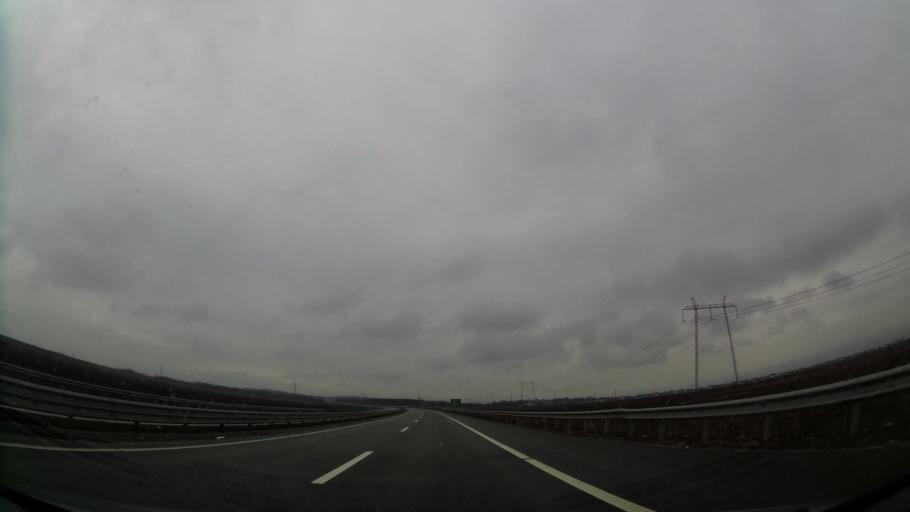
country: XK
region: Ferizaj
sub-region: Komuna e Ferizajt
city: Ferizaj
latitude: 42.3885
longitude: 21.1999
